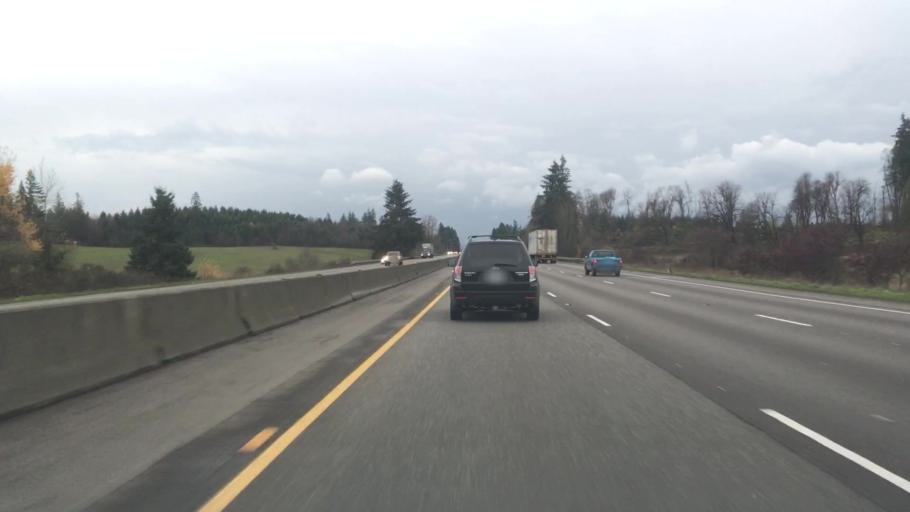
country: US
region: Washington
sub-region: Thurston County
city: Tumwater
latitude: 46.9141
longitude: -122.9506
